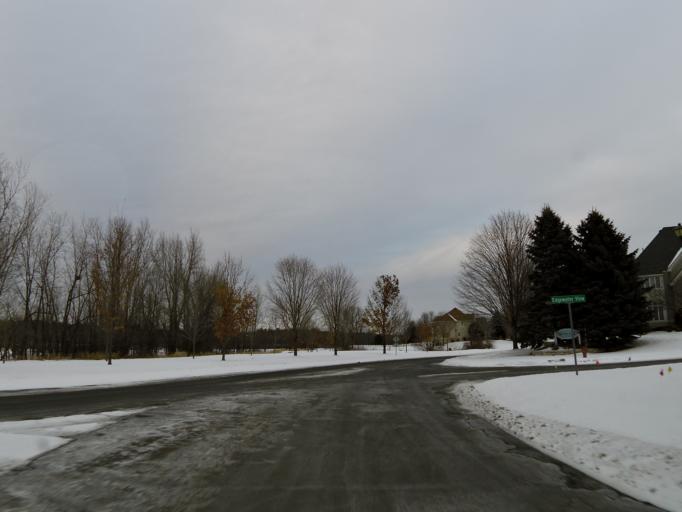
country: US
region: Minnesota
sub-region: Washington County
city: Woodbury
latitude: 44.9032
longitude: -92.9091
